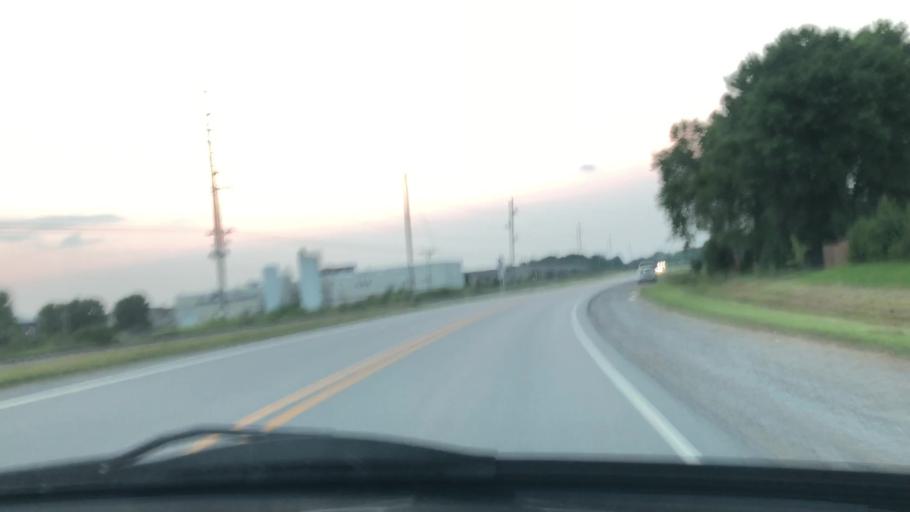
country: US
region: Iowa
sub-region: Johnson County
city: North Liberty
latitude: 41.7617
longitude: -91.6114
